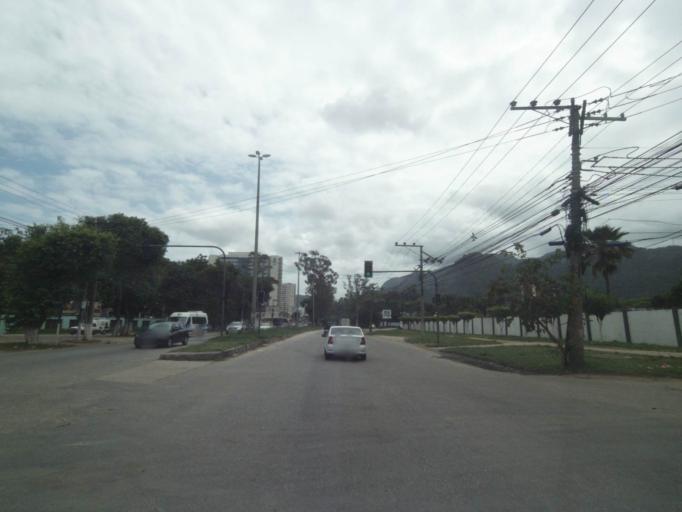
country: BR
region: Rio de Janeiro
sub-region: Nilopolis
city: Nilopolis
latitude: -22.9618
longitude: -43.3971
